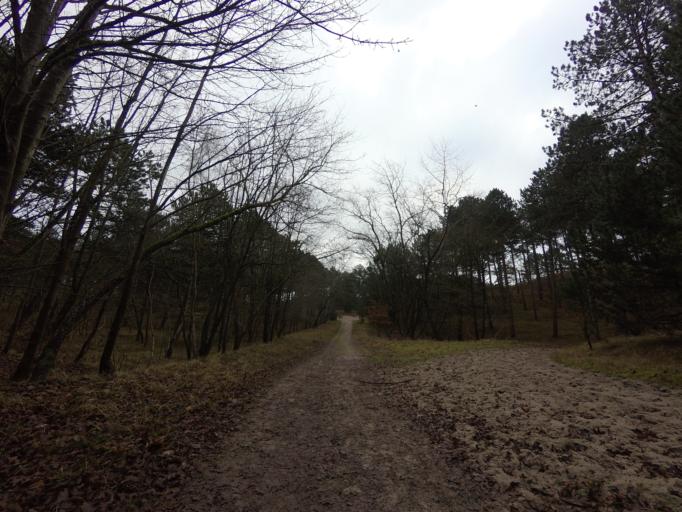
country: NL
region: Zeeland
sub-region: Schouwen-Duiveland
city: Burgh
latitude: 51.6857
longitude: 3.6942
